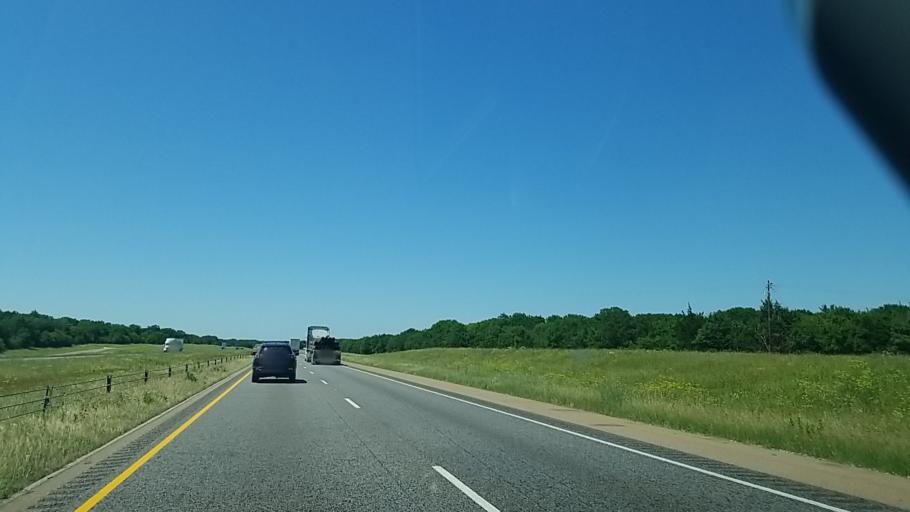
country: US
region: Texas
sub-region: Freestone County
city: Fairfield
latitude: 31.6103
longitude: -96.1564
